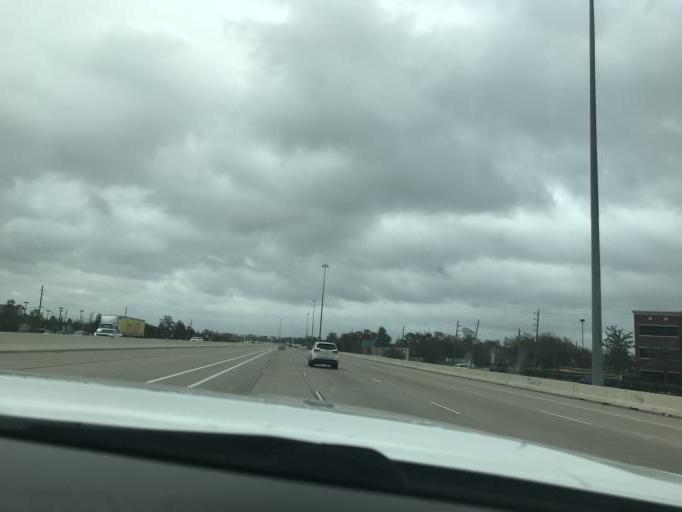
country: US
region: Texas
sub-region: Fort Bend County
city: Greatwood
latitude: 29.5627
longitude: -95.6834
